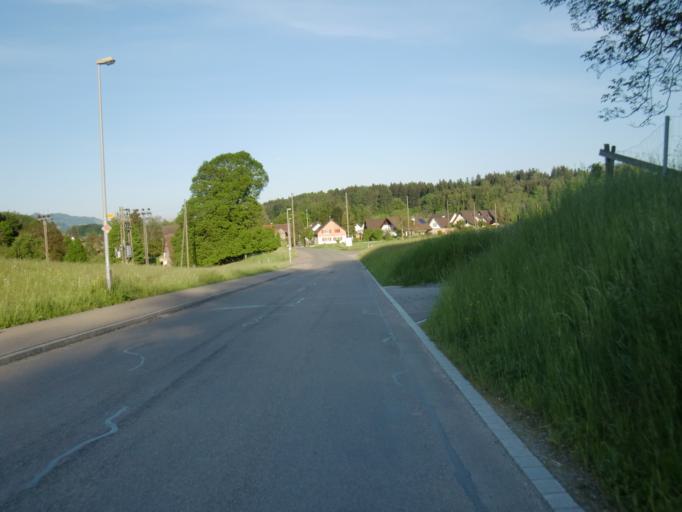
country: CH
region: Zurich
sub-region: Bezirk Hinwil
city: Binzikon
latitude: 47.2792
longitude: 8.7645
